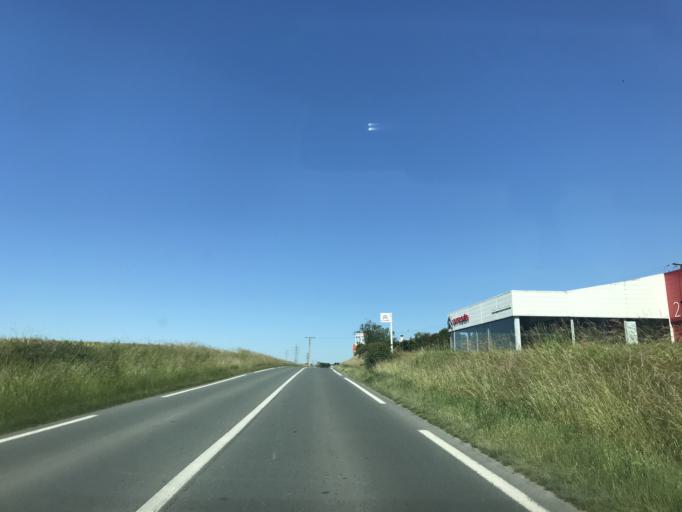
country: FR
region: Poitou-Charentes
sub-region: Departement de la Charente-Maritime
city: Pons
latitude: 45.5730
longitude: -0.5528
